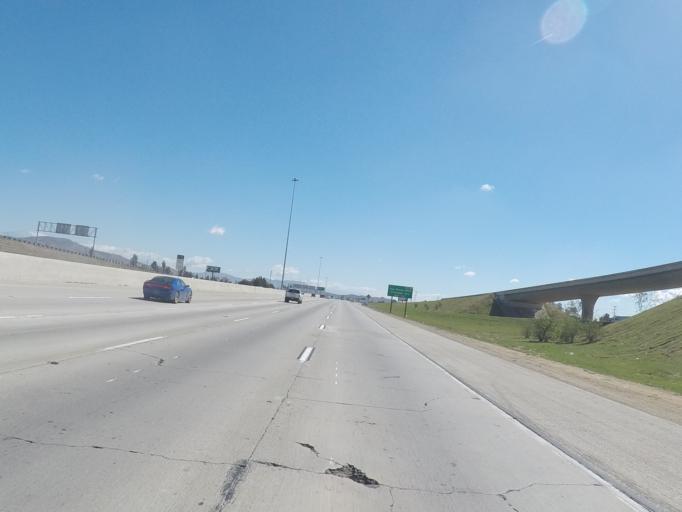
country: US
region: California
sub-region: Riverside County
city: Mira Loma
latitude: 34.0210
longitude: -117.5481
